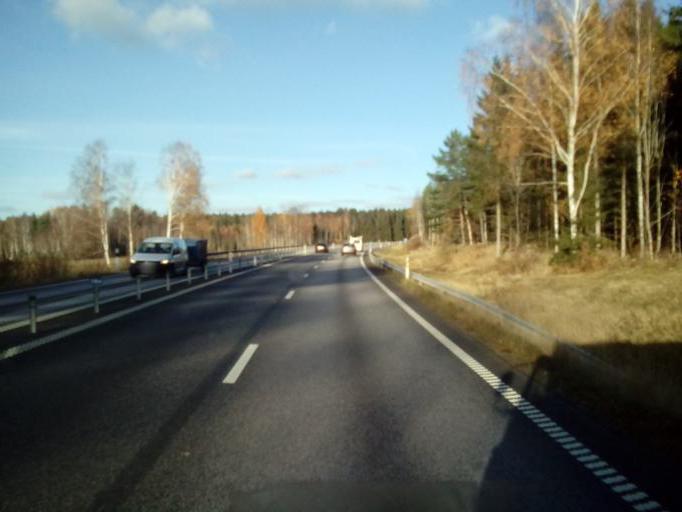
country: SE
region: Kalmar
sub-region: Vimmerby Kommun
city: Vimmerby
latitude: 57.7006
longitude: 16.0170
